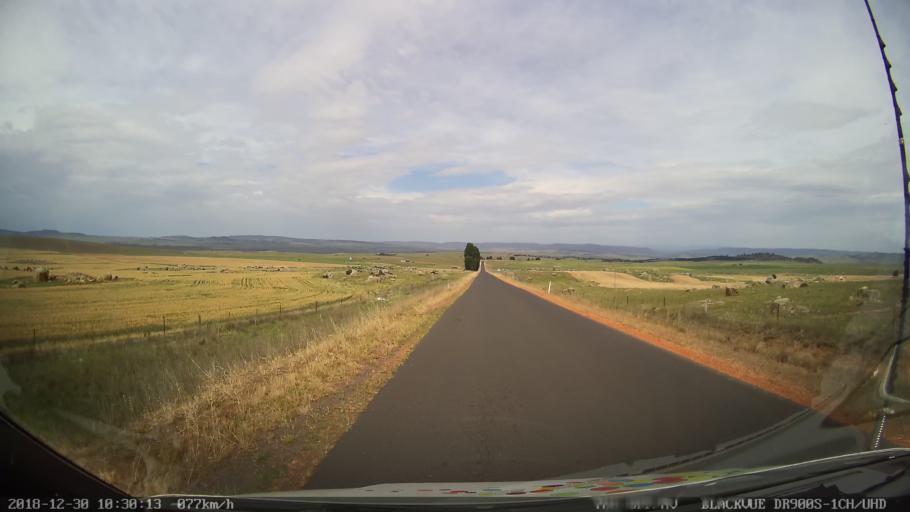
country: AU
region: New South Wales
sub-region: Snowy River
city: Berridale
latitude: -36.5032
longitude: 148.8983
